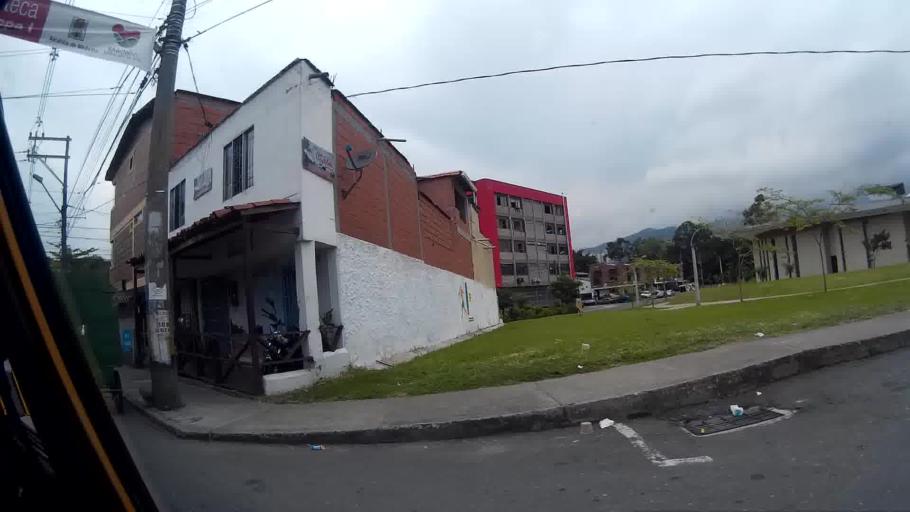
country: CO
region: Antioquia
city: Itagui
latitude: 6.2206
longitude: -75.5864
